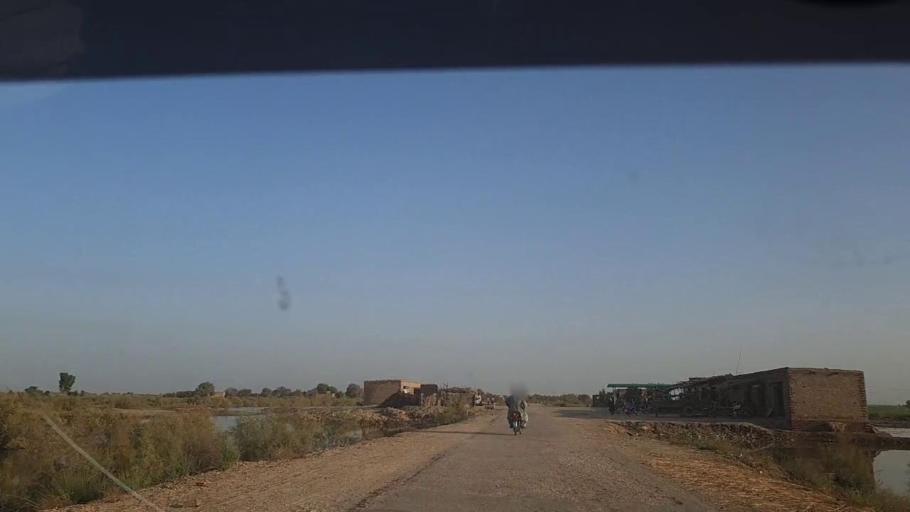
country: PK
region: Sindh
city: Thul
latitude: 28.1500
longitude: 68.8867
